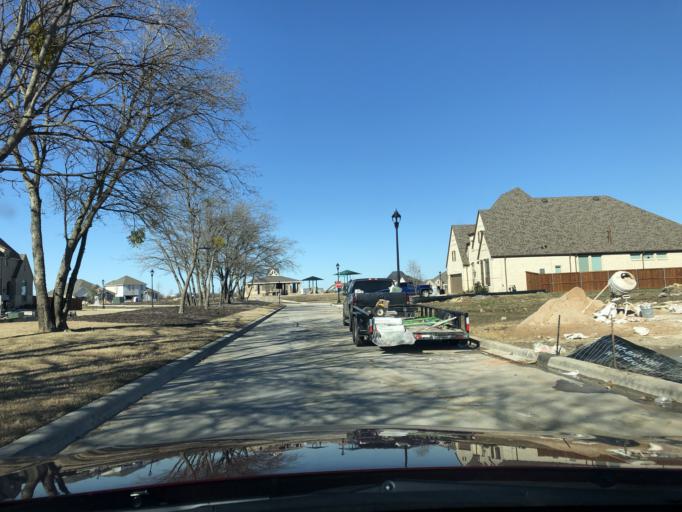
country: US
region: Texas
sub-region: Tarrant County
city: Haslet
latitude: 32.9477
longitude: -97.3980
